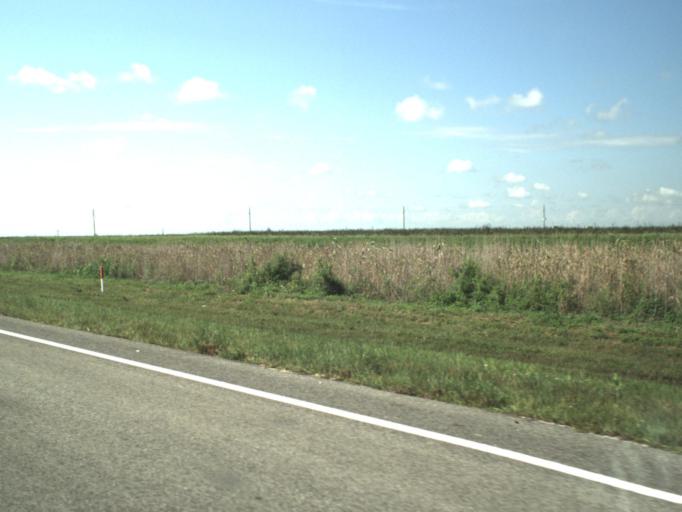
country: US
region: Florida
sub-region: Broward County
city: Coral Springs
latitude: 26.3681
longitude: -80.5637
